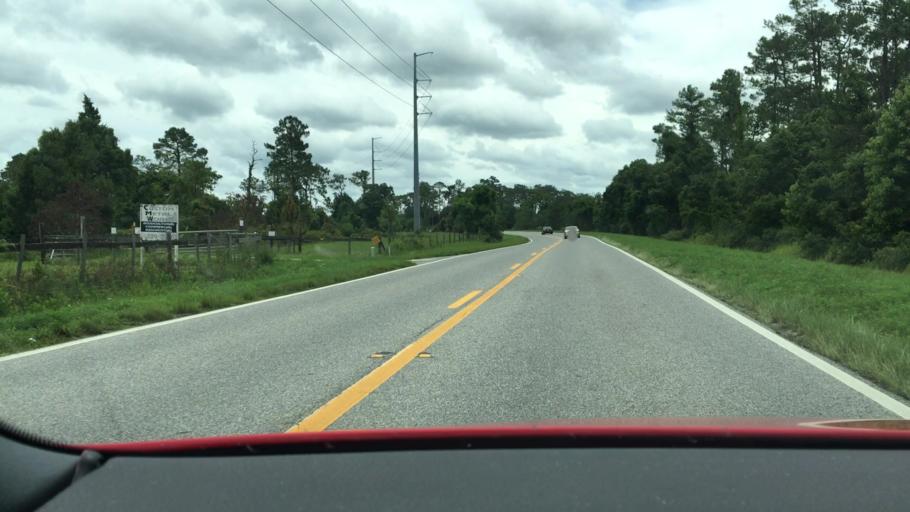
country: US
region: Florida
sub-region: Lake County
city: Eustis
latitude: 28.8709
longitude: -81.6628
